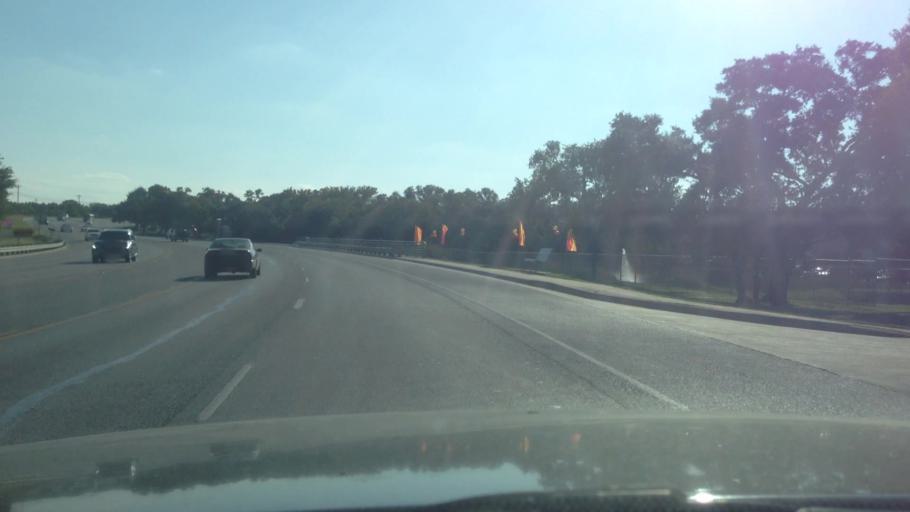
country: US
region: Texas
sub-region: Hays County
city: San Marcos
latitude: 29.8558
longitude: -97.9714
